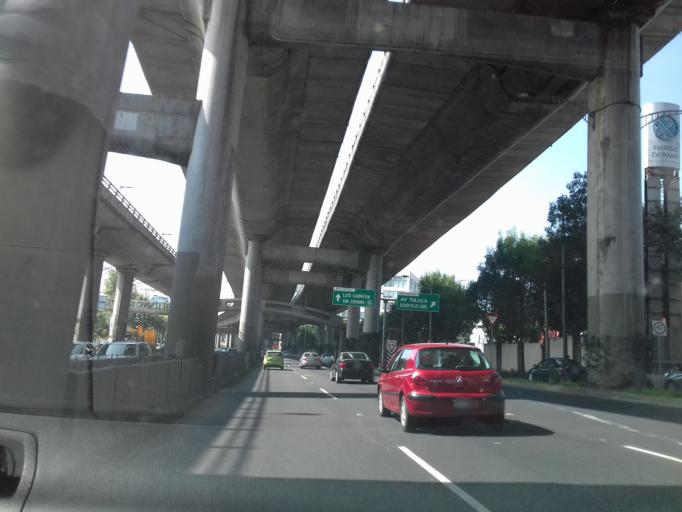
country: MX
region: Mexico City
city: Alvaro Obregon
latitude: 19.3547
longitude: -99.2000
